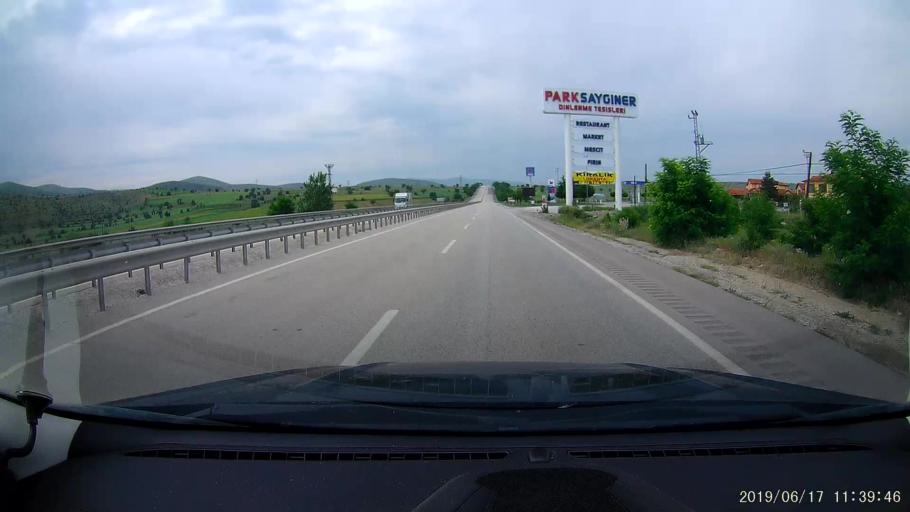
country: TR
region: Cankiri
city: Kursunlu
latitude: 40.8385
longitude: 33.3670
